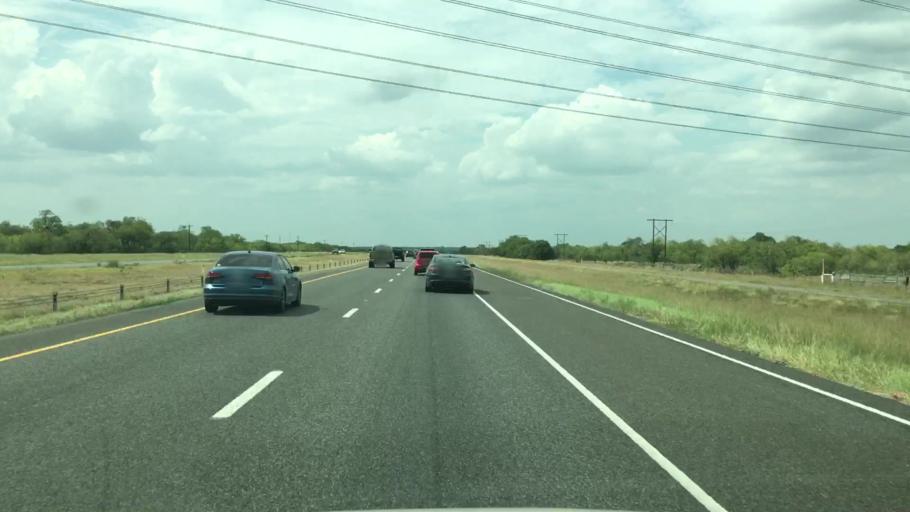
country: US
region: Texas
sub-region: Atascosa County
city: Pleasanton
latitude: 28.8215
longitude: -98.3619
